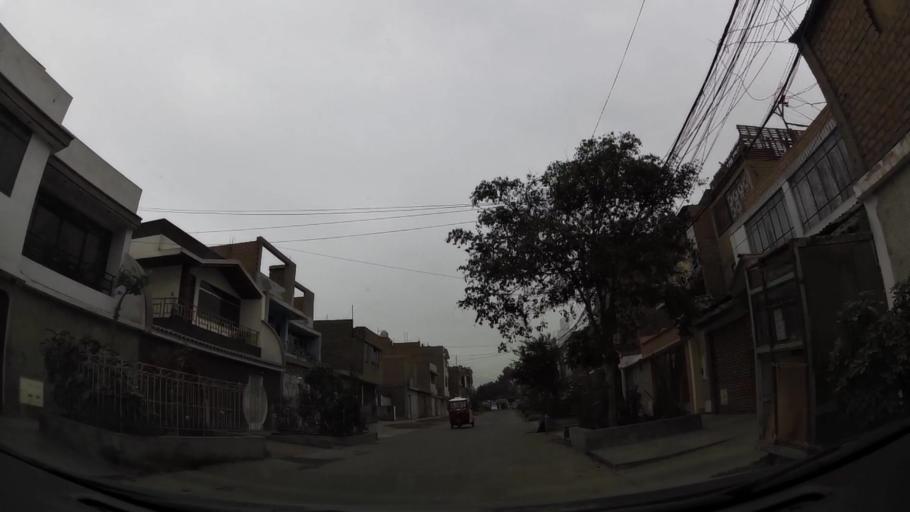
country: PE
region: Lima
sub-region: Lima
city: Independencia
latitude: -11.9662
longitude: -77.0584
